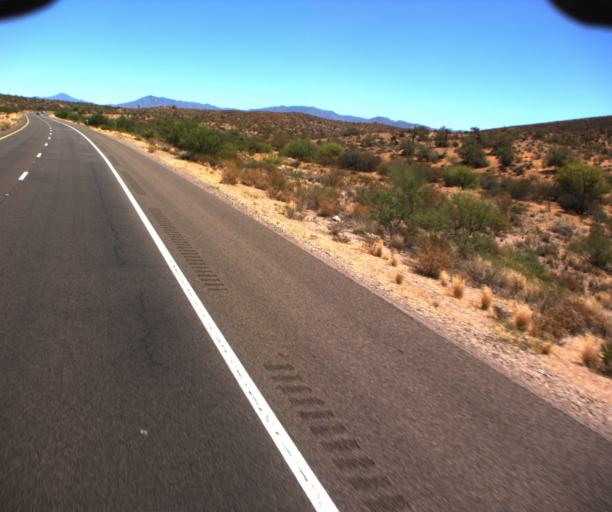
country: US
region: Arizona
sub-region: Maricopa County
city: Fountain Hills
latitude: 33.6135
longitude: -111.5720
